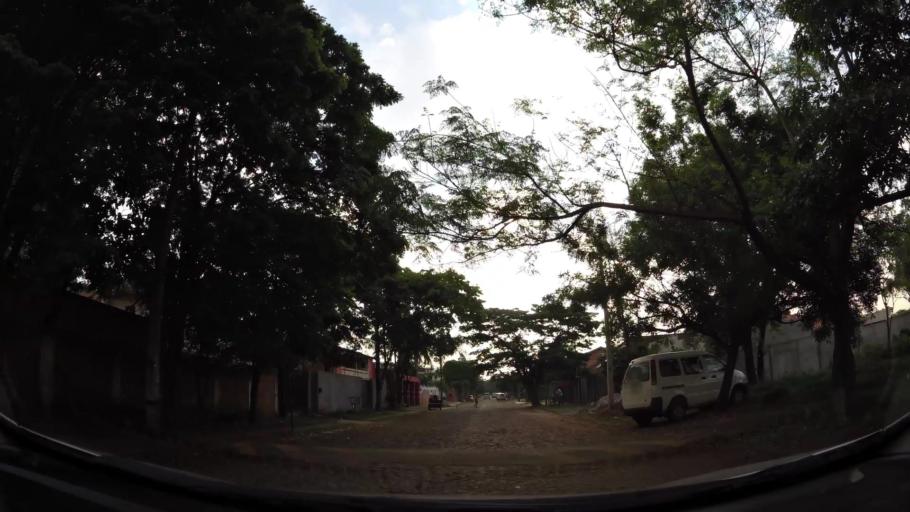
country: PY
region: Alto Parana
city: Presidente Franco
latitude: -25.5207
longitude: -54.6307
